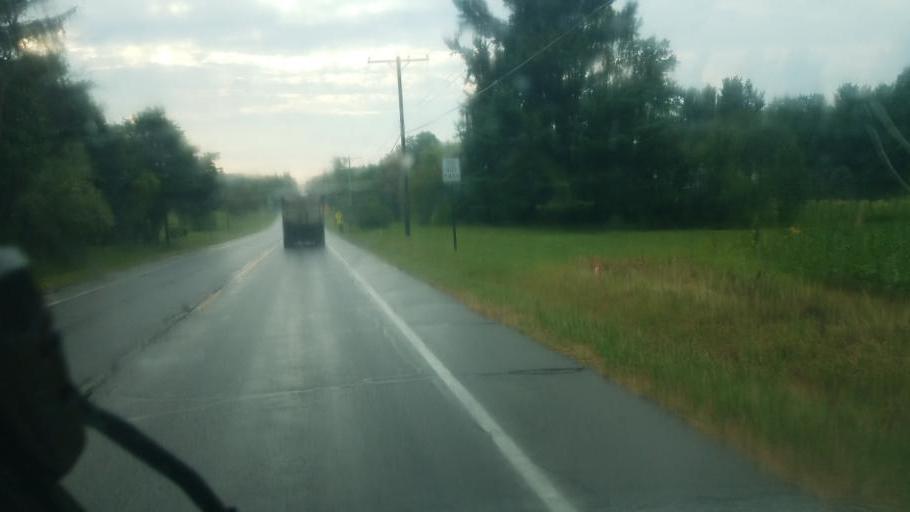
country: US
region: Ohio
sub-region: Portage County
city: Hiram
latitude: 41.3842
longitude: -81.1320
